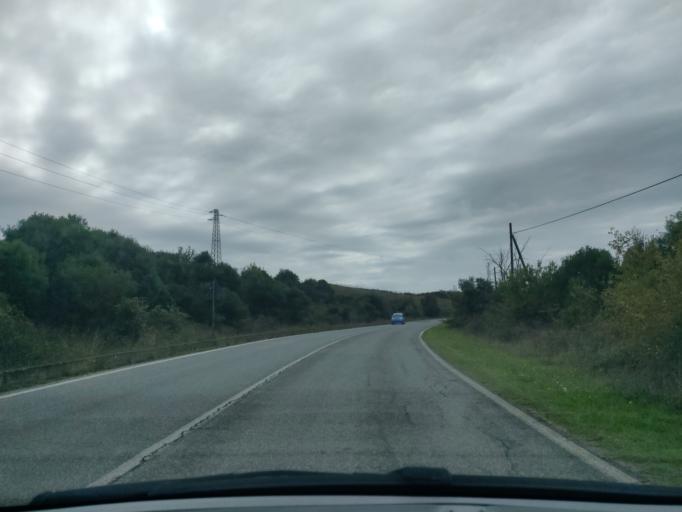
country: IT
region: Latium
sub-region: Citta metropolitana di Roma Capitale
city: Allumiere
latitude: 42.1167
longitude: 11.8615
